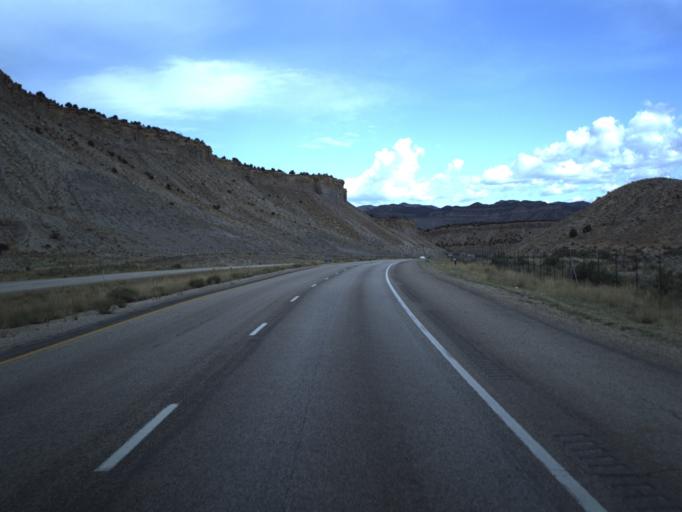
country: US
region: Utah
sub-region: Carbon County
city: Carbonville
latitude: 39.6265
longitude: -110.8601
